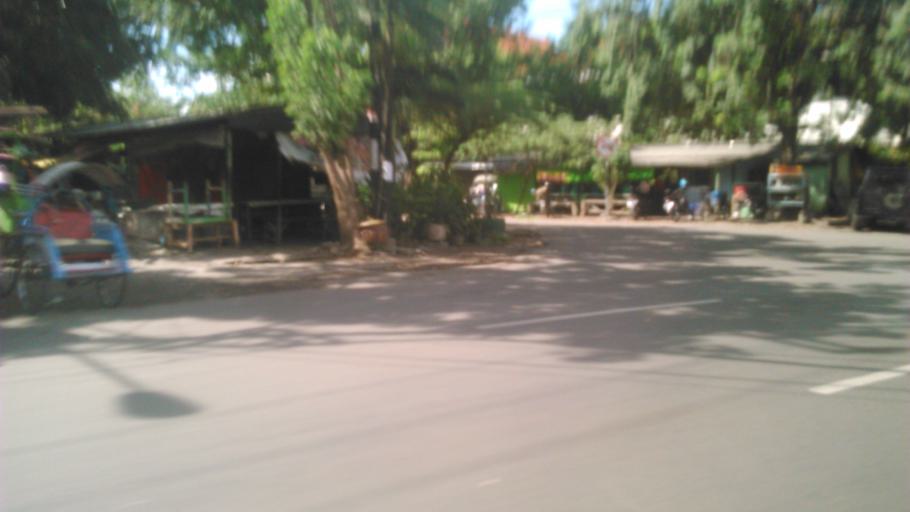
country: ID
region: East Java
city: Pacarkeling
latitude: -7.2549
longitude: 112.7545
